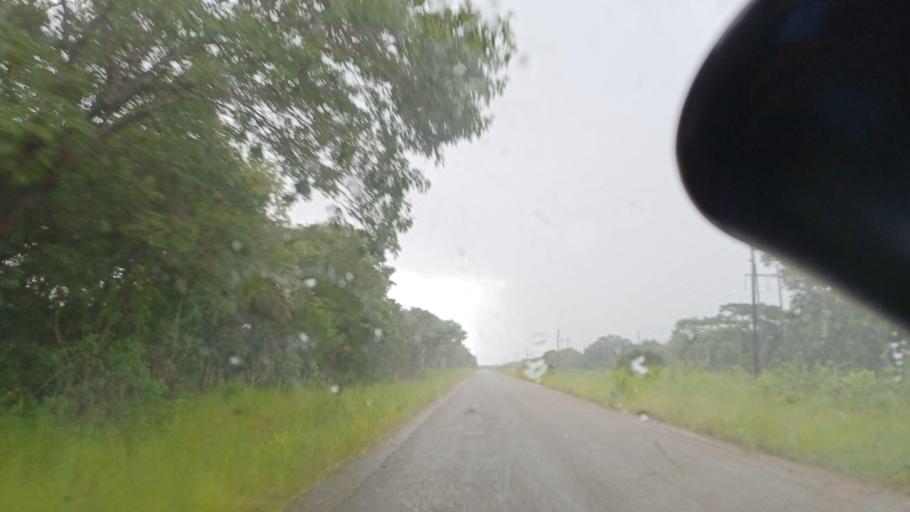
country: ZM
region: North-Western
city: Kasempa
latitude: -13.0911
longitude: 25.9384
